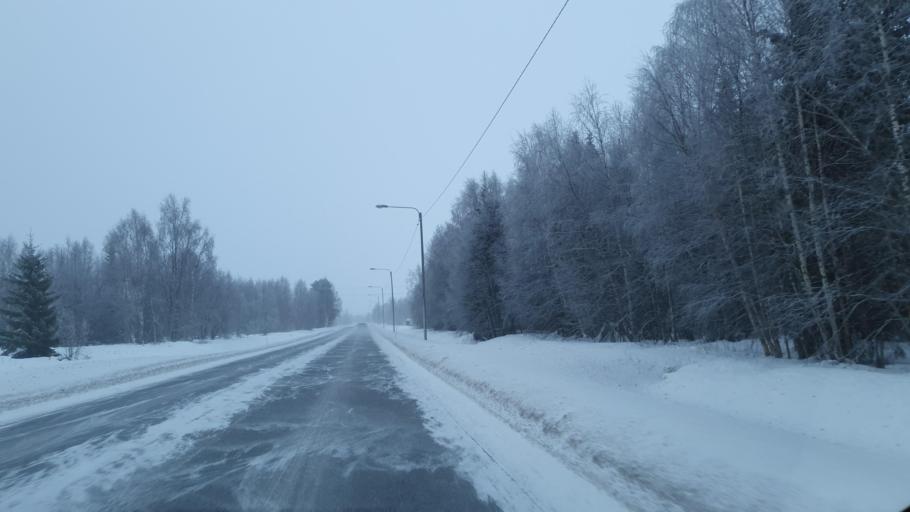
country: FI
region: Lapland
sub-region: Kemi-Tornio
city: Tornio
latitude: 66.0755
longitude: 23.9811
